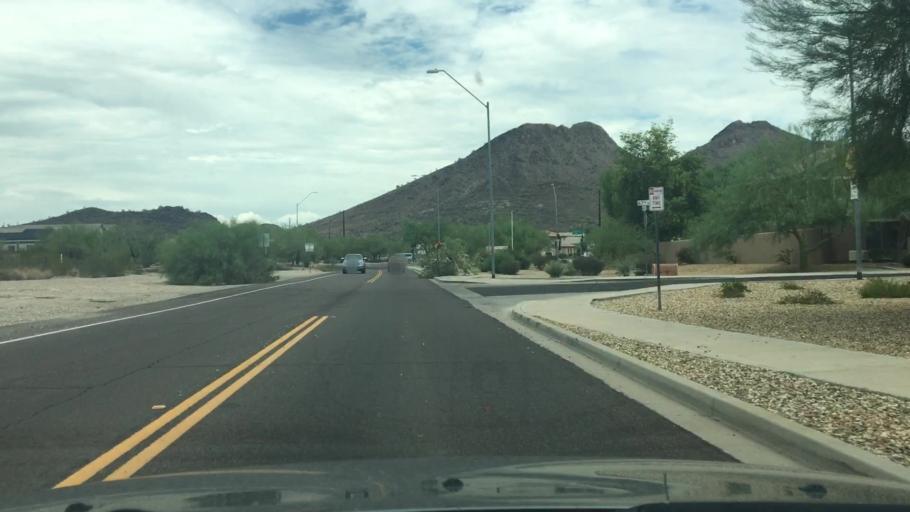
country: US
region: Arizona
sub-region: Maricopa County
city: Sun City
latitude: 33.7250
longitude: -112.2046
